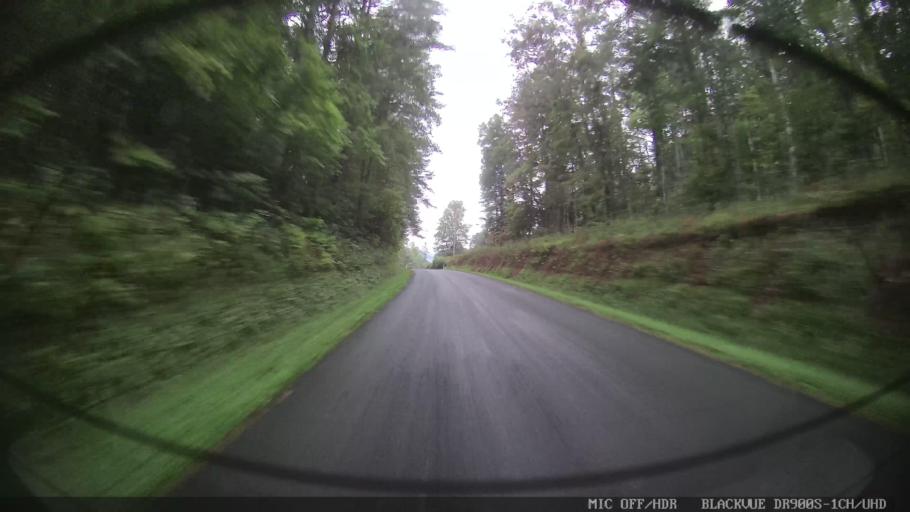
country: US
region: Georgia
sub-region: Gilmer County
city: Ellijay
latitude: 34.7802
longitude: -84.5439
